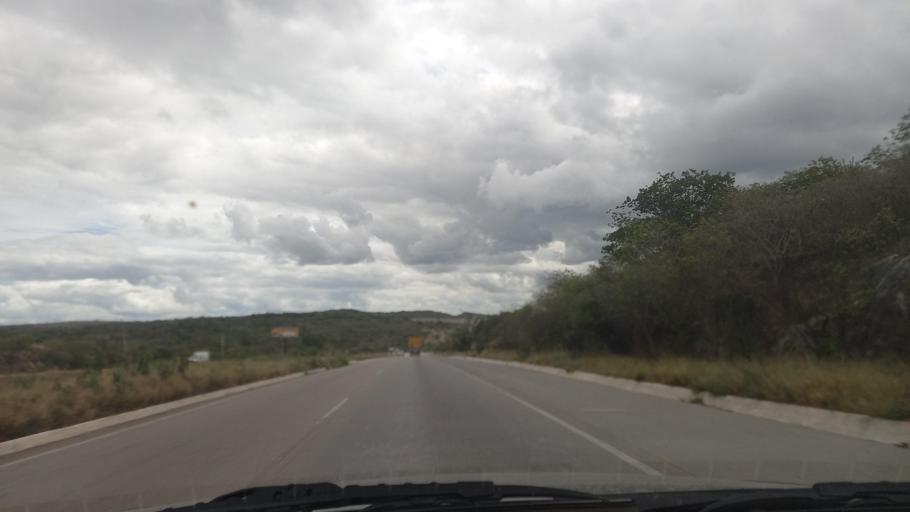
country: BR
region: Pernambuco
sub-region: Caruaru
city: Caruaru
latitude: -8.3212
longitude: -36.0867
